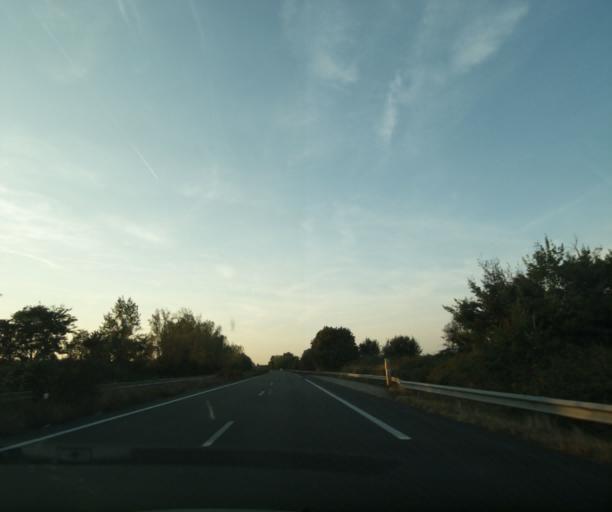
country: FR
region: Aquitaine
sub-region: Departement du Lot-et-Garonne
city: Tonneins
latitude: 44.3619
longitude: 0.2457
